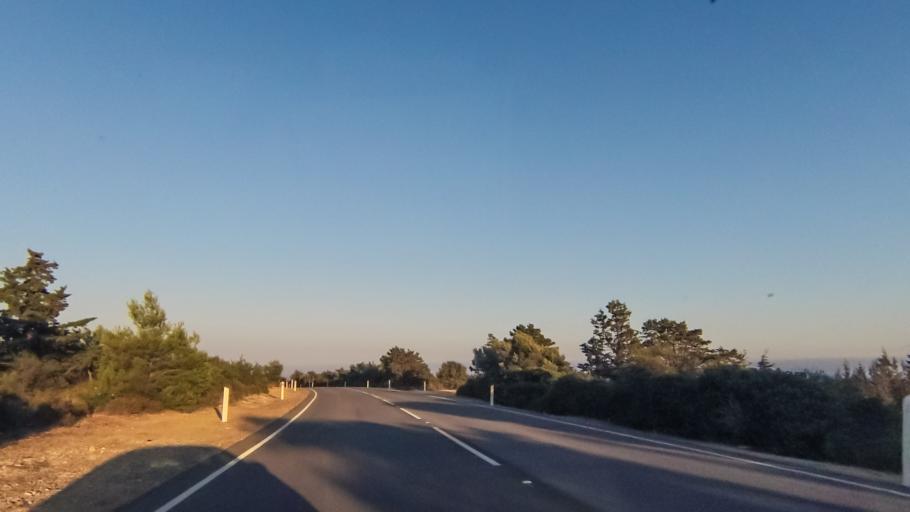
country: CY
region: Limassol
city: Sotira
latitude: 34.6717
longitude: 32.8576
